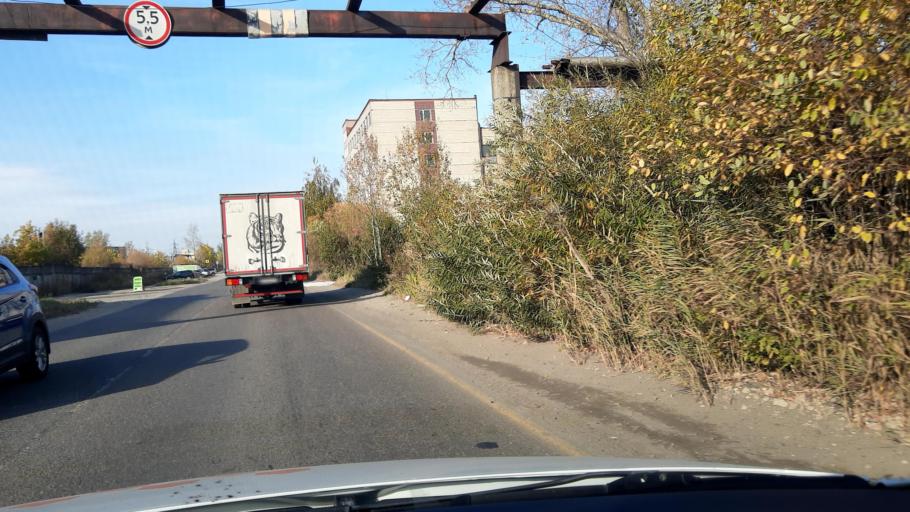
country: RU
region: Moskovskaya
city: Elektrostal'
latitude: 55.7717
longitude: 38.4713
